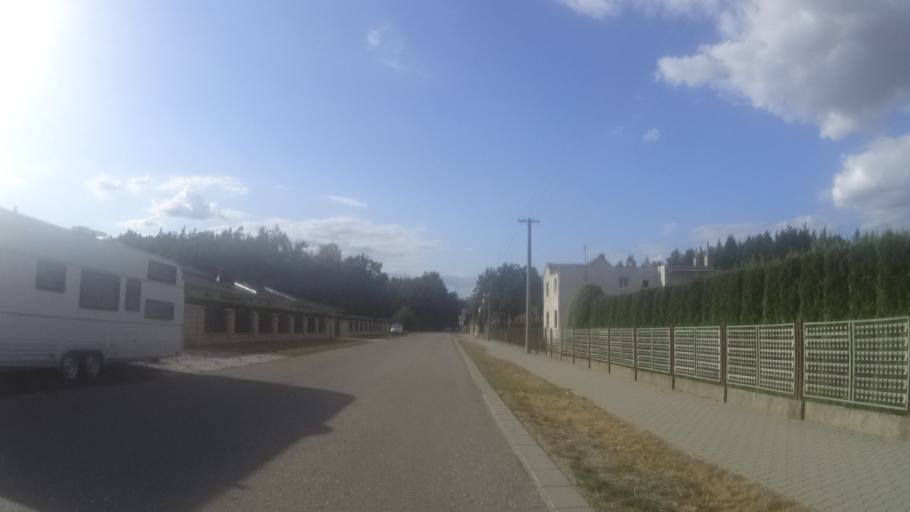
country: CZ
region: Kralovehradecky
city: Trebechovice pod Orebem
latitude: 50.1924
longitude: 16.0040
